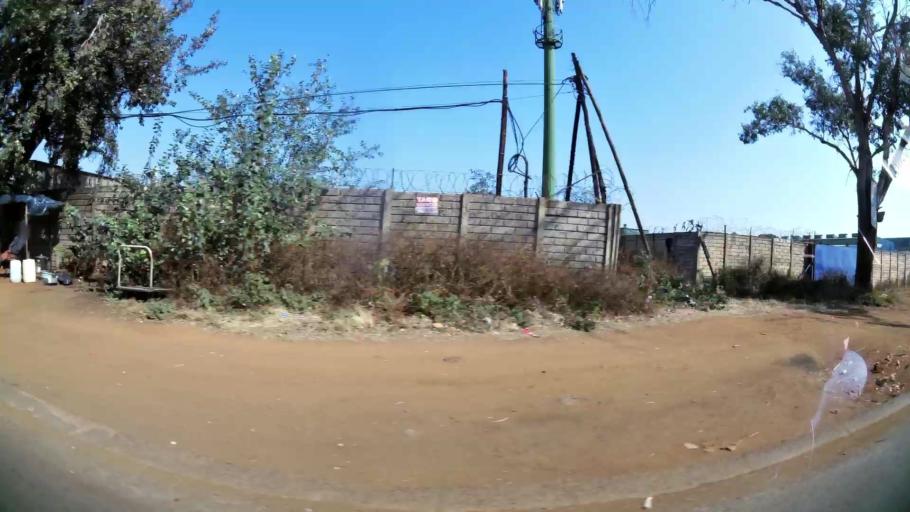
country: ZA
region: Gauteng
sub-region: Ekurhuleni Metropolitan Municipality
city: Boksburg
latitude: -26.1730
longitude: 28.2119
